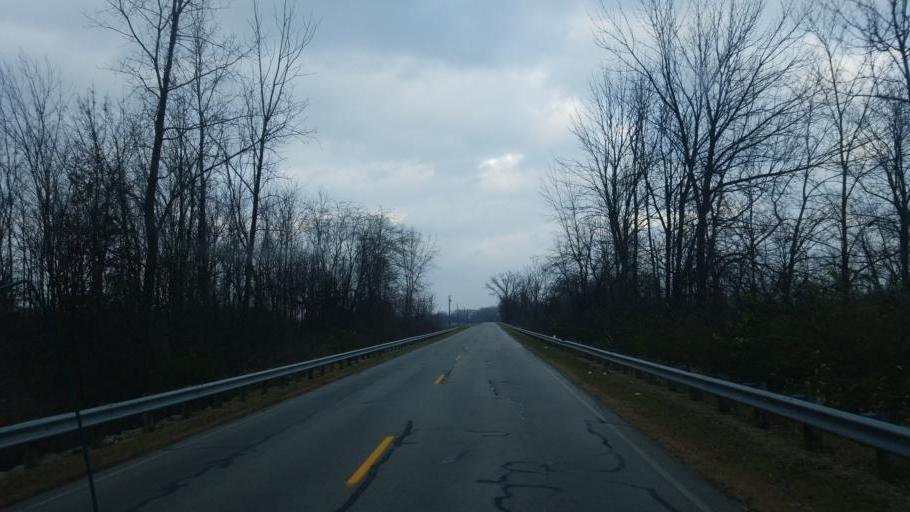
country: US
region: Ohio
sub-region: Mercer County
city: Celina
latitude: 40.5107
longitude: -84.5858
